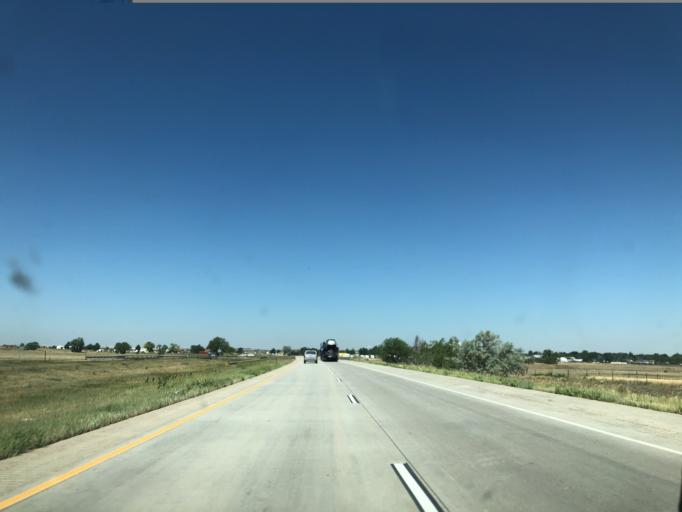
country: US
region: Colorado
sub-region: Adams County
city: Strasburg
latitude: 39.7333
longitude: -104.3121
